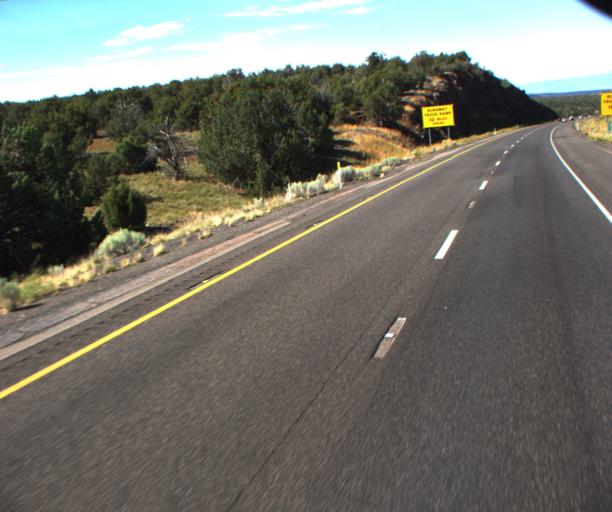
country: US
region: Arizona
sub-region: Yavapai County
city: Village of Oak Creek (Big Park)
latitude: 34.7920
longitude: -111.6020
